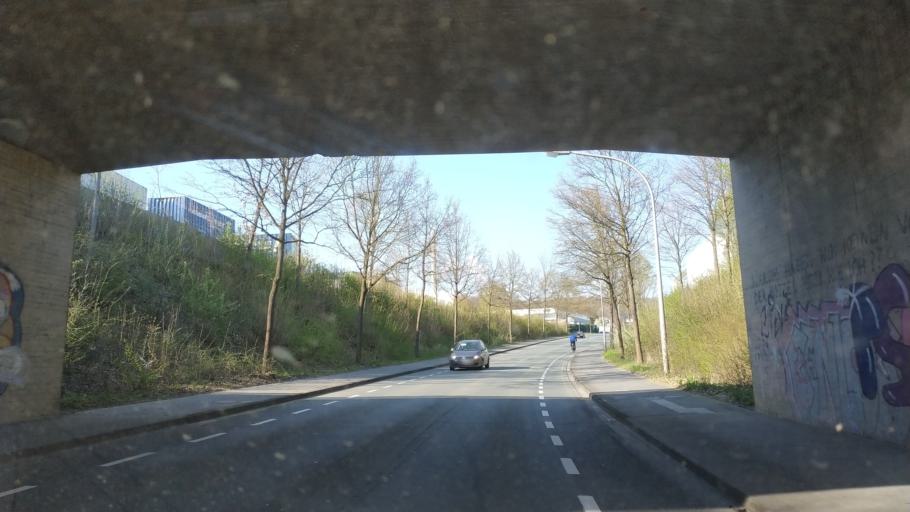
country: DE
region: North Rhine-Westphalia
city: Ibbenburen
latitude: 52.2701
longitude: 7.7462
